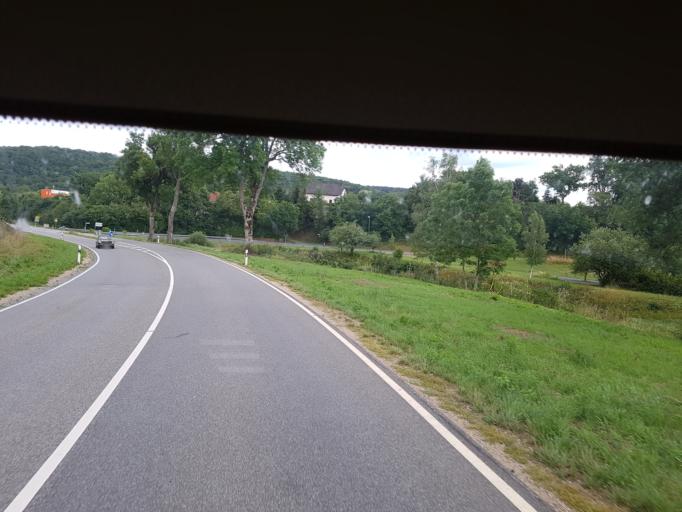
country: DE
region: Rheinland-Pfalz
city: Gerolstein
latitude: 50.2145
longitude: 6.6309
